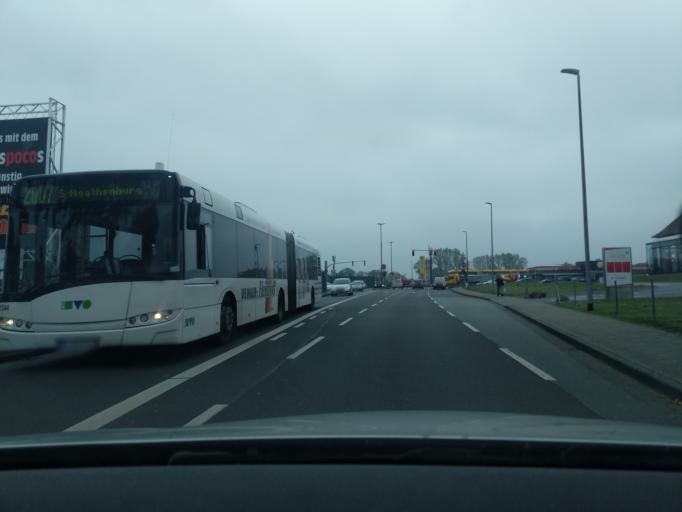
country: DE
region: Lower Saxony
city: Stade
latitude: 53.5957
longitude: 9.4232
